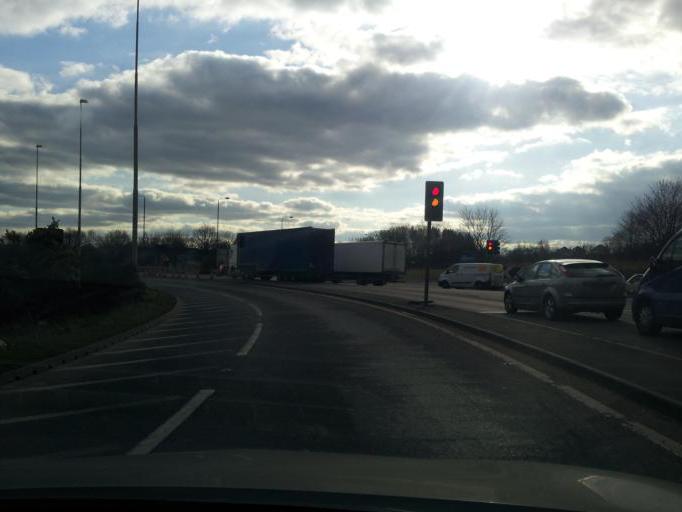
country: GB
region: England
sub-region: Derbyshire
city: Pinxton
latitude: 53.1021
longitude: -1.3221
